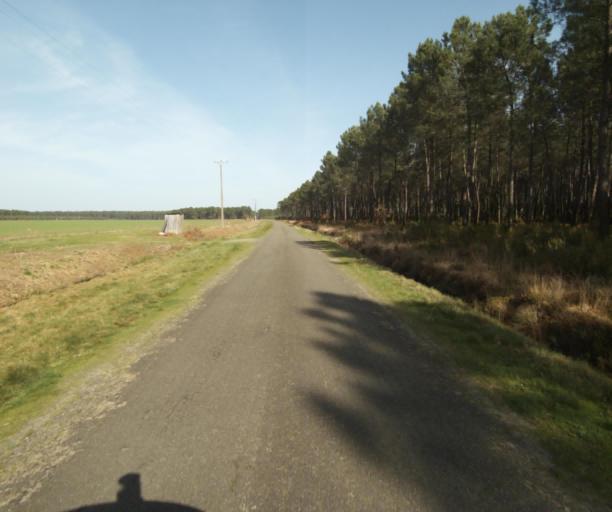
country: FR
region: Aquitaine
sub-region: Departement des Landes
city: Roquefort
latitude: 44.1675
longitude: -0.1983
